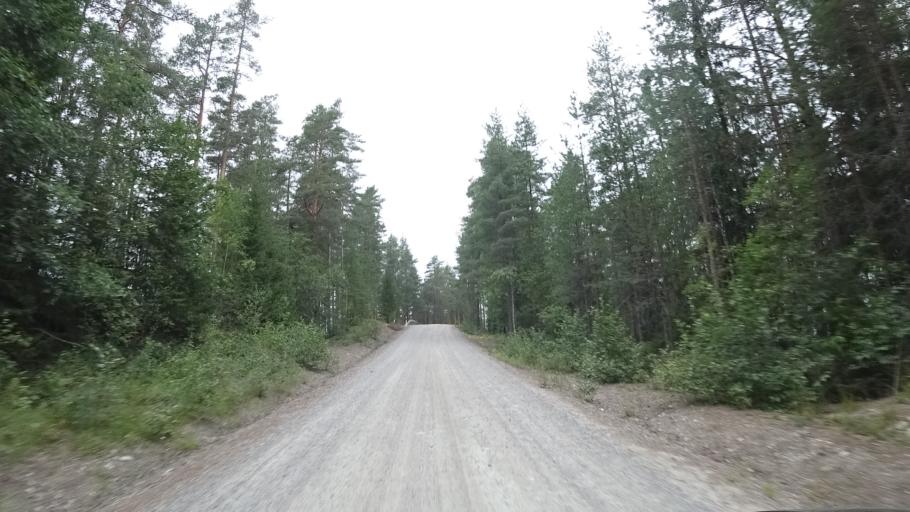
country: FI
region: North Karelia
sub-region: Pielisen Karjala
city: Lieksa
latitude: 63.2326
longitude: 30.3695
